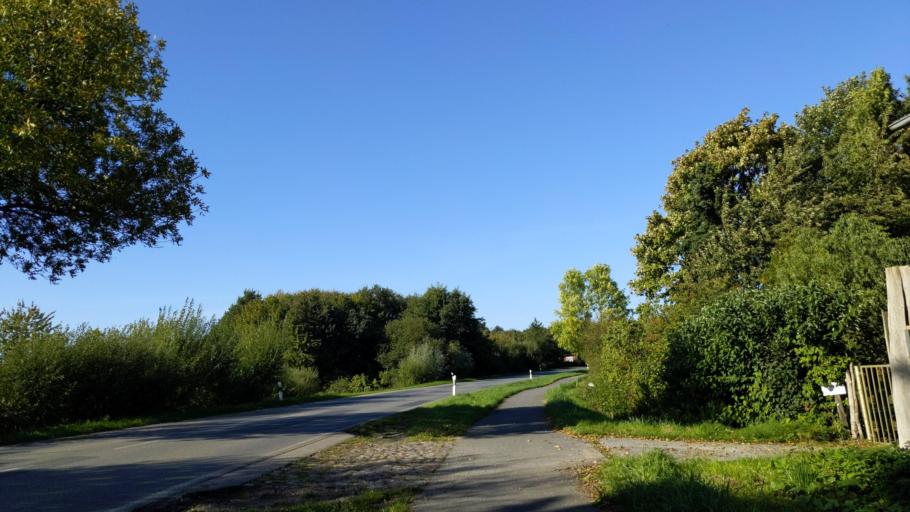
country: DE
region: Schleswig-Holstein
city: Ahrensbok
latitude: 53.9767
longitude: 10.5879
